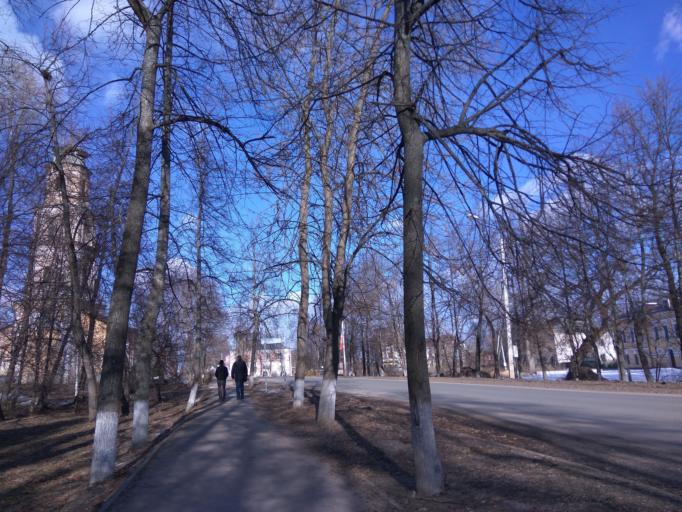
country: RU
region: Jaroslavl
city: Rostov
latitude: 57.1869
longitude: 39.4251
